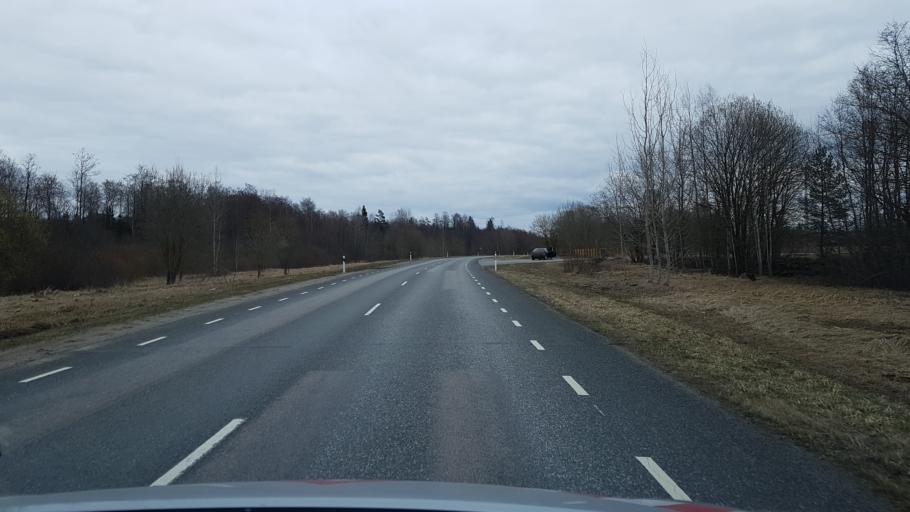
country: EE
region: Ida-Virumaa
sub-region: Narva-Joesuu linn
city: Narva-Joesuu
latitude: 59.3506
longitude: 28.0405
